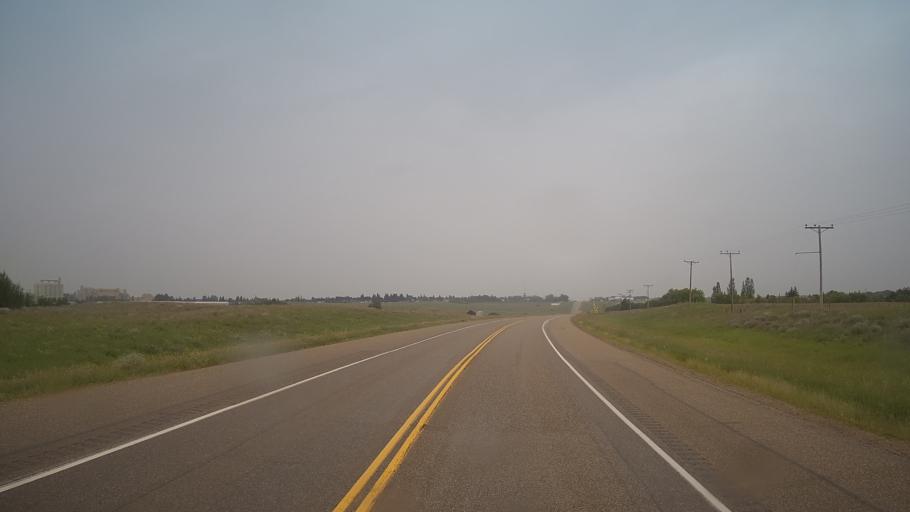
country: CA
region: Saskatchewan
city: Biggar
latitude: 52.0565
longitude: -107.9499
